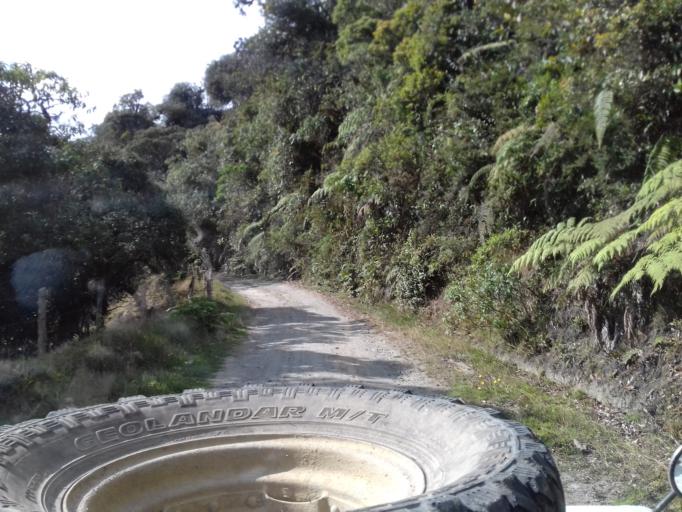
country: CO
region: Quindio
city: Salento
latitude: 4.5523
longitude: -75.5085
